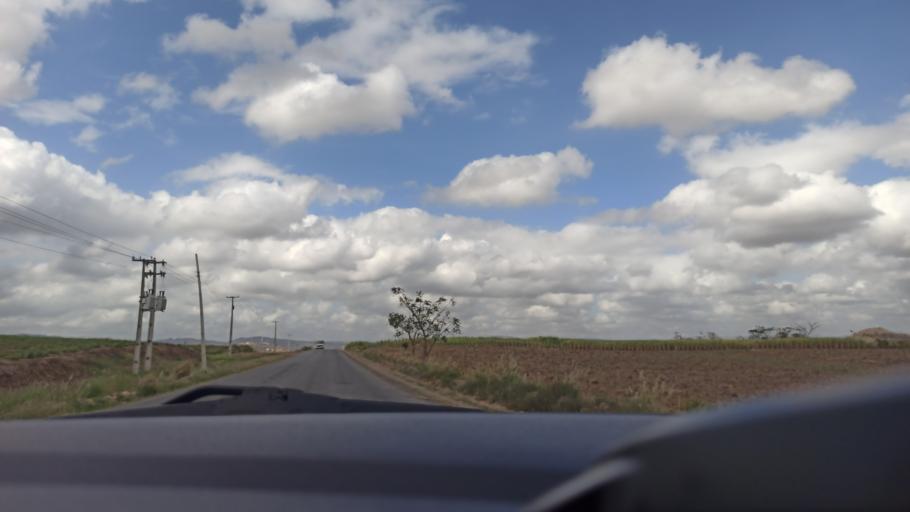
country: BR
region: Pernambuco
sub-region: Timbauba
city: Timbauba
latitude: -7.4816
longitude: -35.2871
